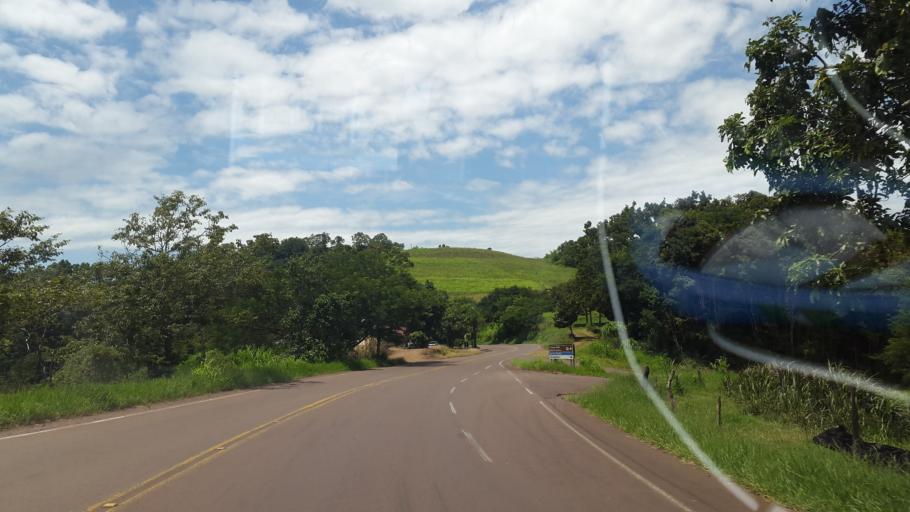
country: BR
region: Rio Grande do Sul
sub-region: Frederico Westphalen
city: Frederico Westphalen
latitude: -27.0591
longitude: -53.4803
